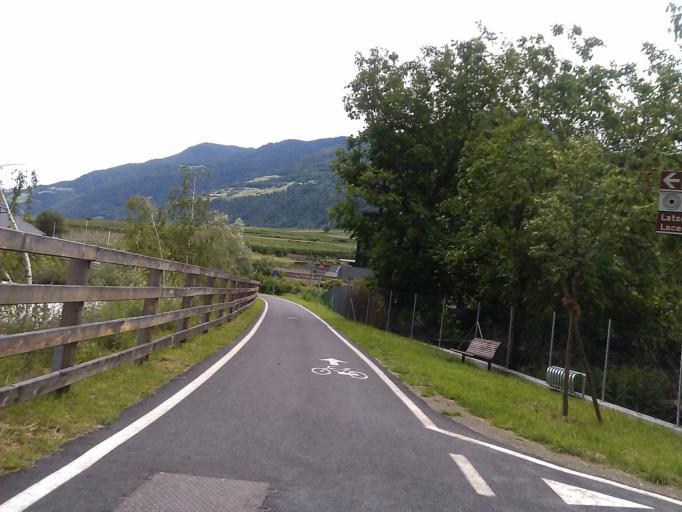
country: IT
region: Trentino-Alto Adige
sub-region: Bolzano
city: Laces
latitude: 46.6211
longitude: 10.8640
